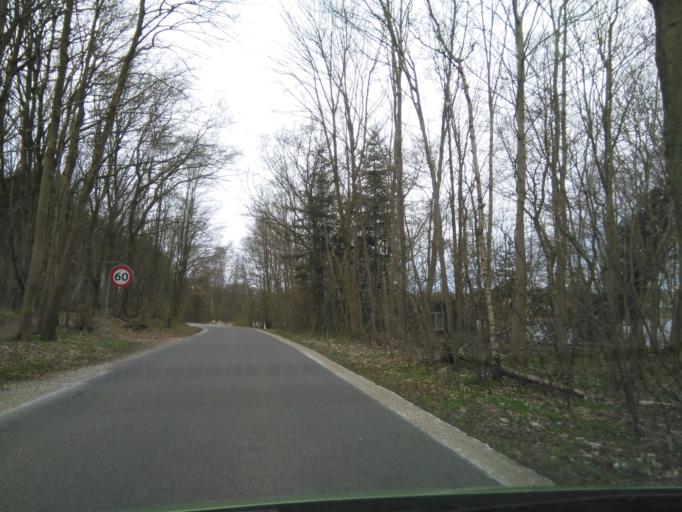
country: DK
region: Central Jutland
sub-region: Skanderborg Kommune
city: Stilling
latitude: 56.0577
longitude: 9.9973
